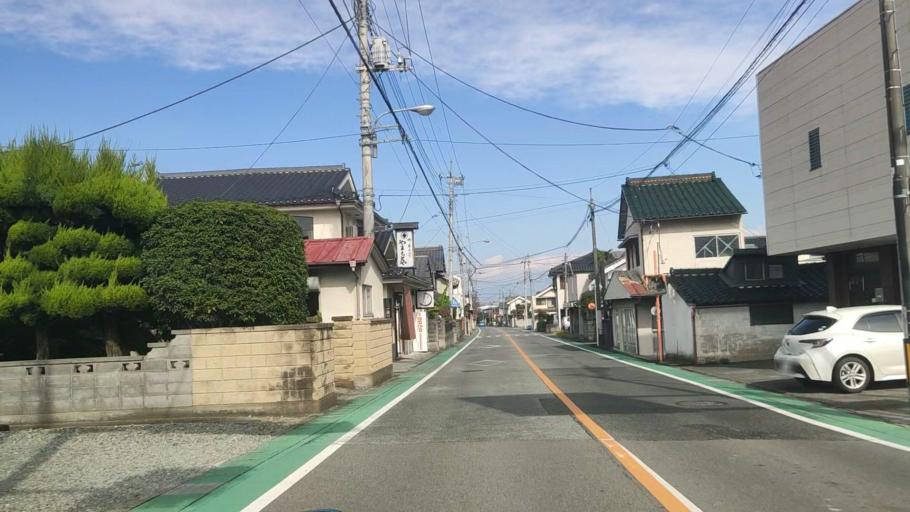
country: JP
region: Yamanashi
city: Ryuo
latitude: 35.5668
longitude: 138.4647
